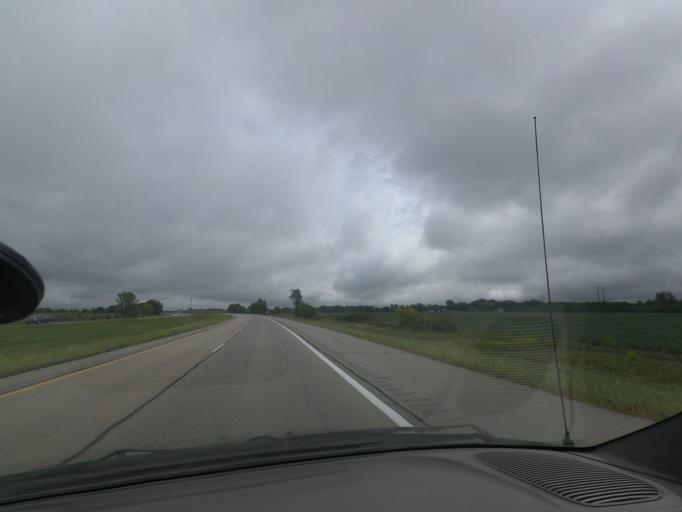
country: US
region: Illinois
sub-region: Piatt County
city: Monticello
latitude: 40.0316
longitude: -88.6045
